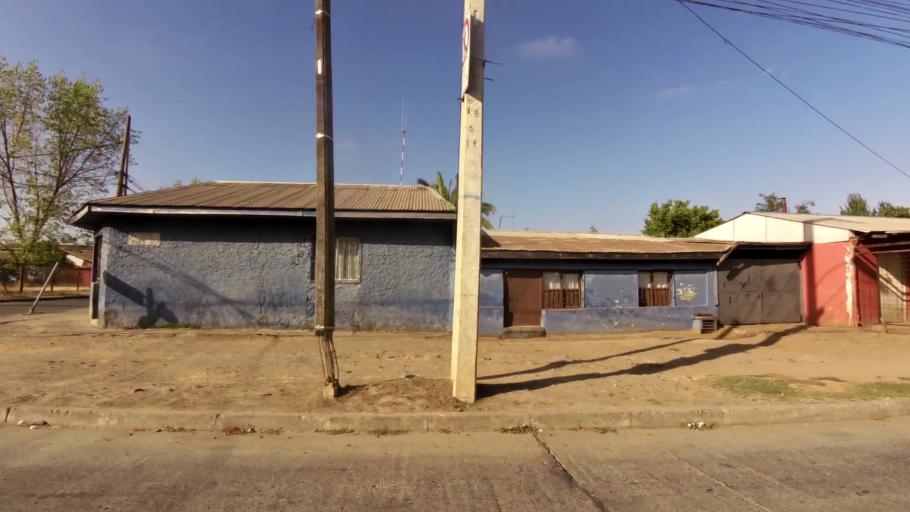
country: CL
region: Maule
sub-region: Provincia de Talca
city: Talca
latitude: -35.4052
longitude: -71.6604
